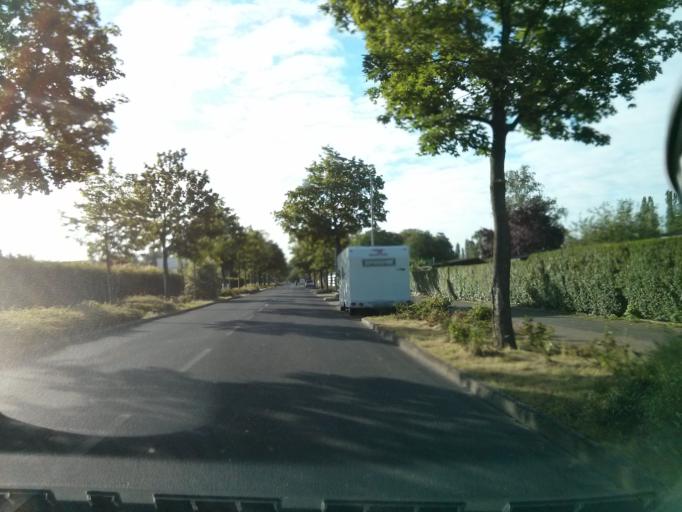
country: DE
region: North Rhine-Westphalia
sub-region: Regierungsbezirk Dusseldorf
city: Krefeld
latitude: 51.3097
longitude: 6.5721
